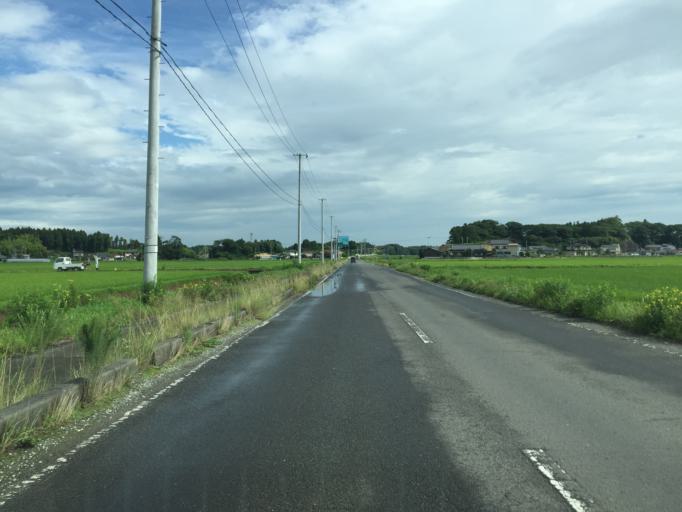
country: JP
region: Miyagi
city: Marumori
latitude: 37.8009
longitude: 140.9567
